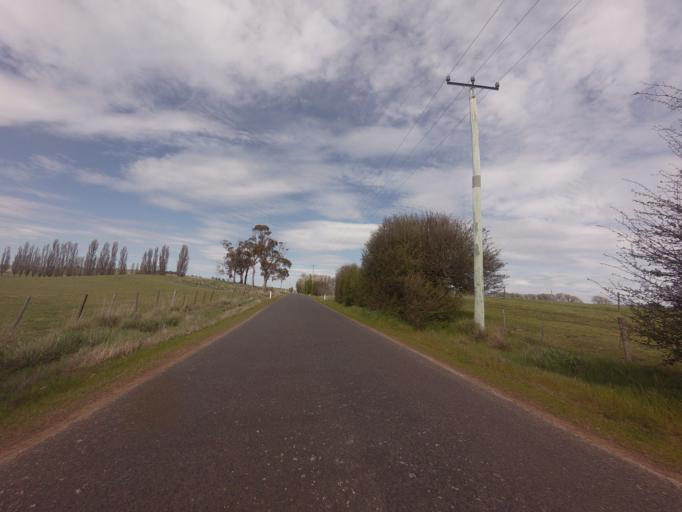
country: AU
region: Tasmania
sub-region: Northern Midlands
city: Evandale
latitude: -41.8767
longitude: 147.3573
